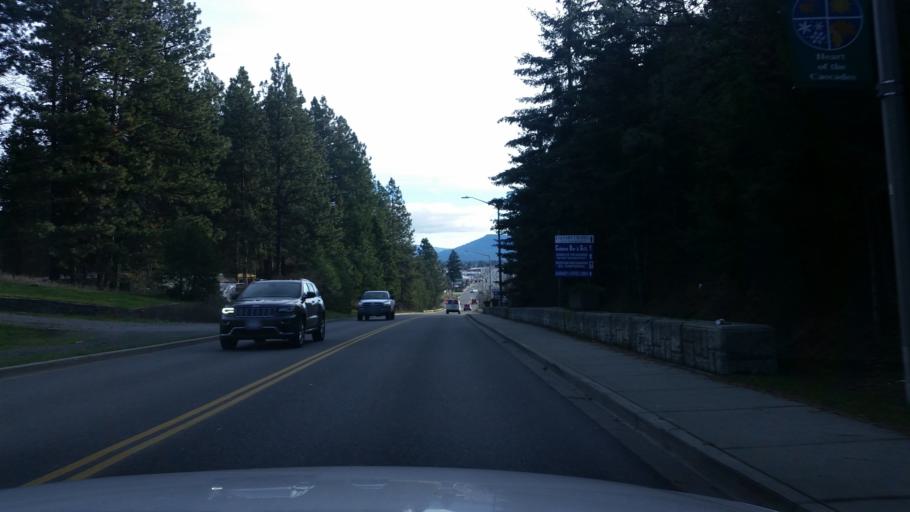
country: US
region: Washington
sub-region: Kittitas County
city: Cle Elum
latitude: 47.1961
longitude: -120.9490
